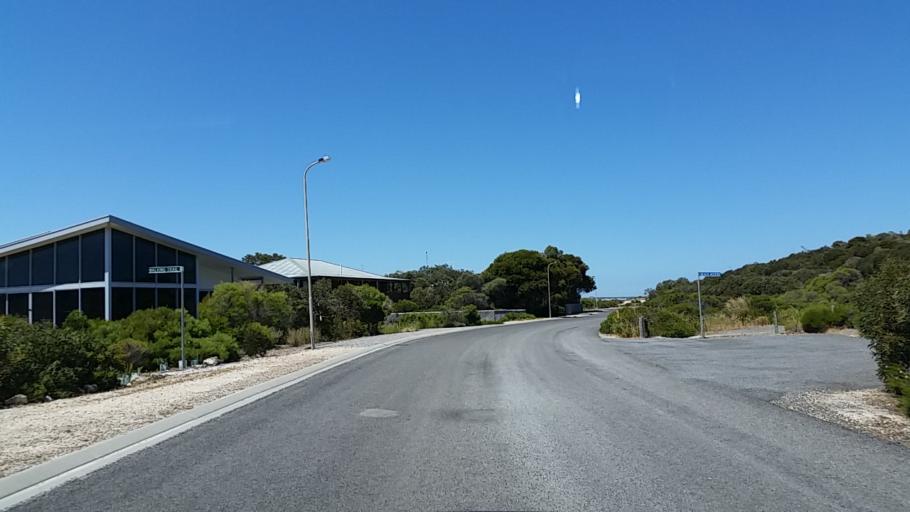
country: AU
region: South Australia
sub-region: Yorke Peninsula
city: Honiton
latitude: -35.2488
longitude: 136.9763
